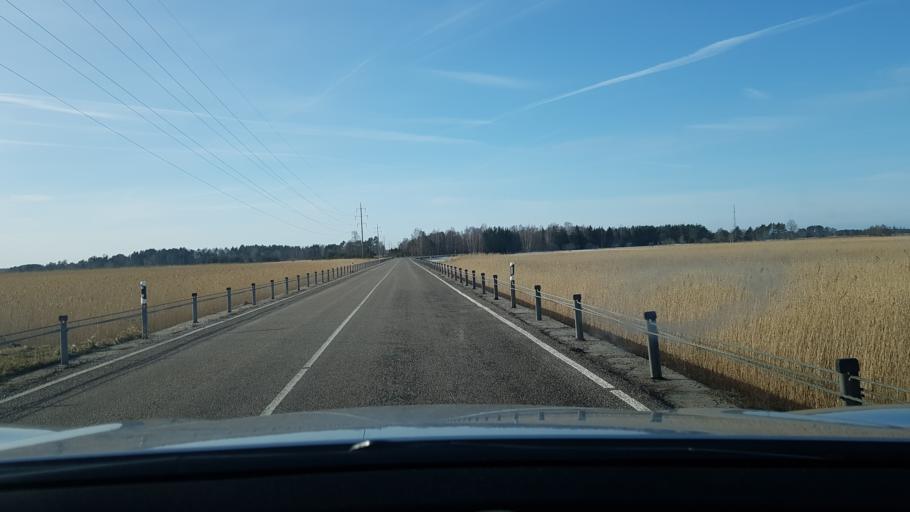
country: EE
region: Saare
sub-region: Orissaare vald
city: Orissaare
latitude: 58.5486
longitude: 23.1324
